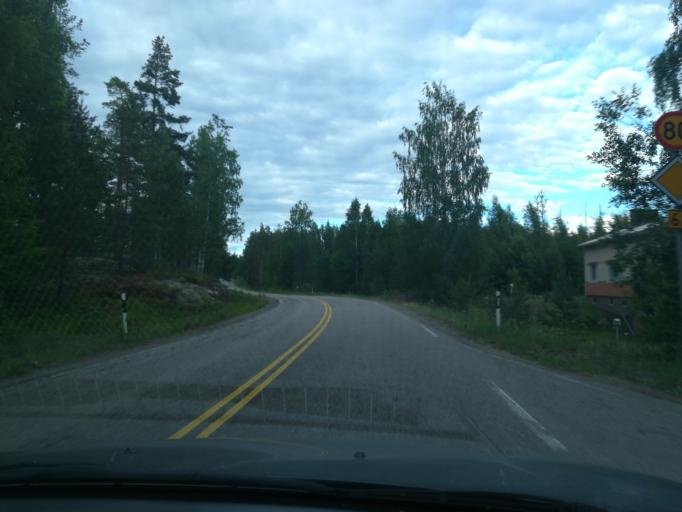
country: FI
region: South Karelia
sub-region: Lappeenranta
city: Savitaipale
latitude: 61.4987
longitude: 27.8303
